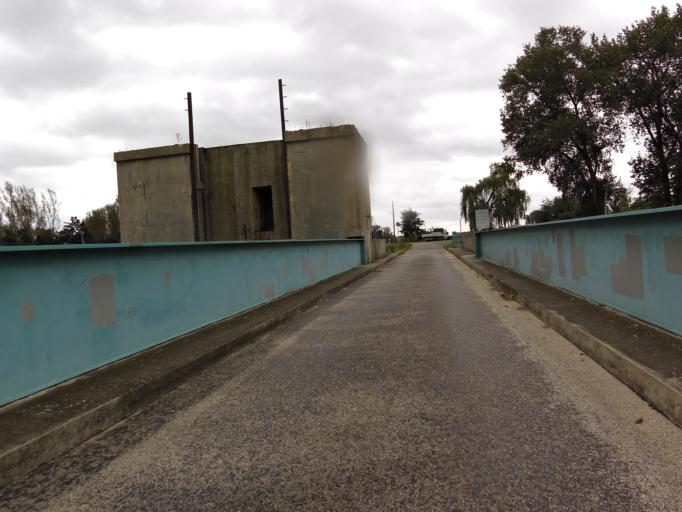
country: DE
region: Saxony-Anhalt
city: Havelberg
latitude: 52.8785
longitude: 12.0082
